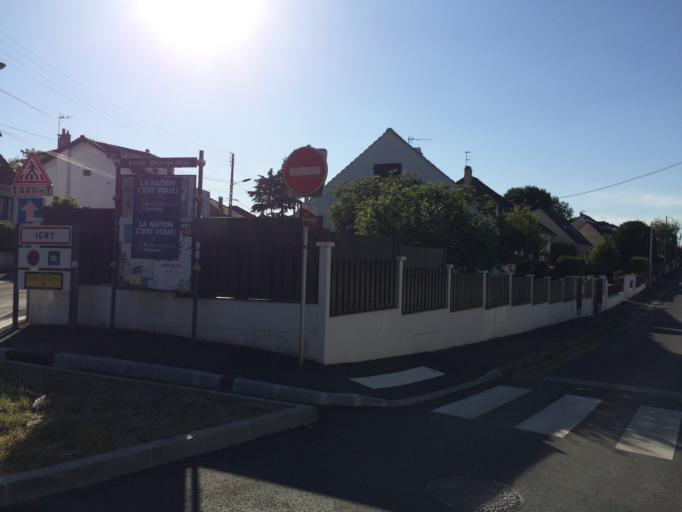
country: FR
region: Ile-de-France
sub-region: Departement de l'Essonne
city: Igny
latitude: 48.7251
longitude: 2.2233
